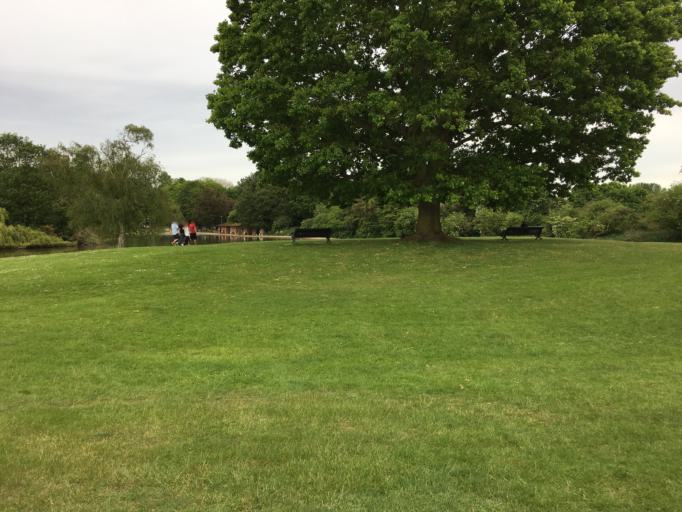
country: GB
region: England
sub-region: Hertfordshire
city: St Albans
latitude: 51.7486
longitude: -0.3509
